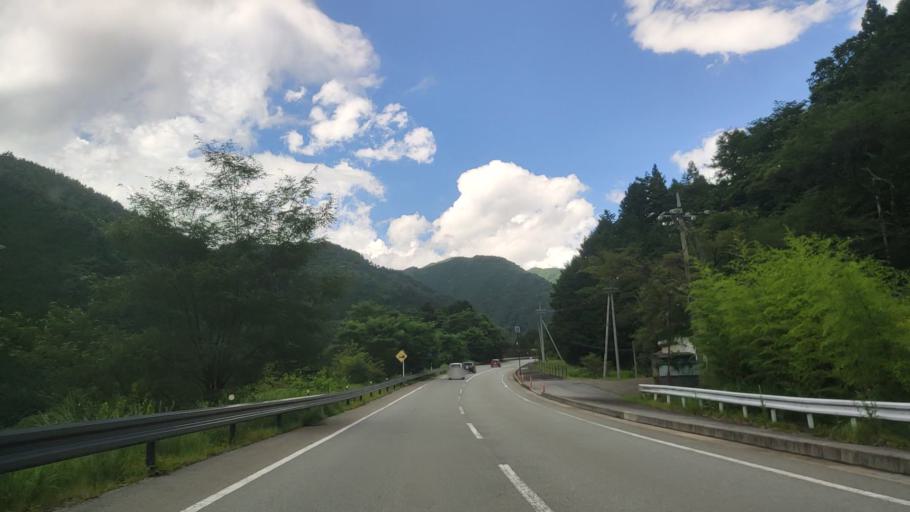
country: JP
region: Yamanashi
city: Enzan
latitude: 35.8092
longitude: 138.7513
